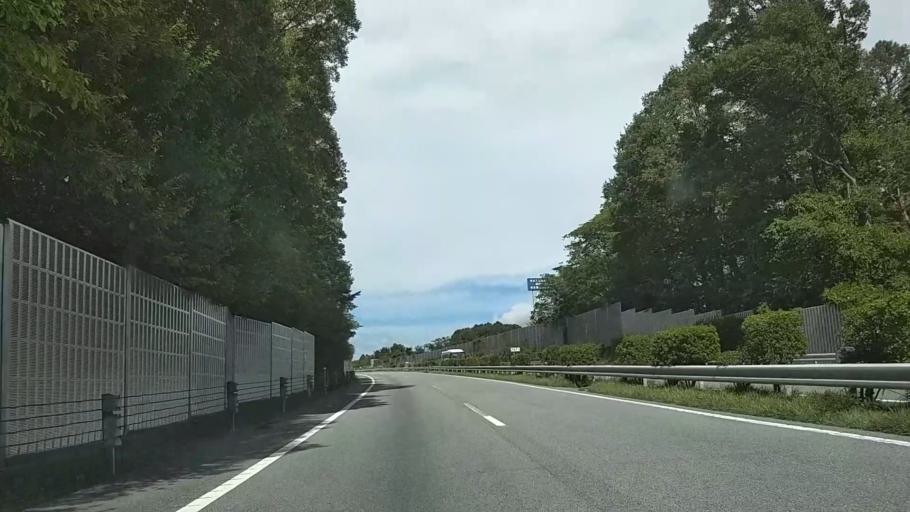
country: JP
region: Yamanashi
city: Nirasaki
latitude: 35.8667
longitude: 138.3231
